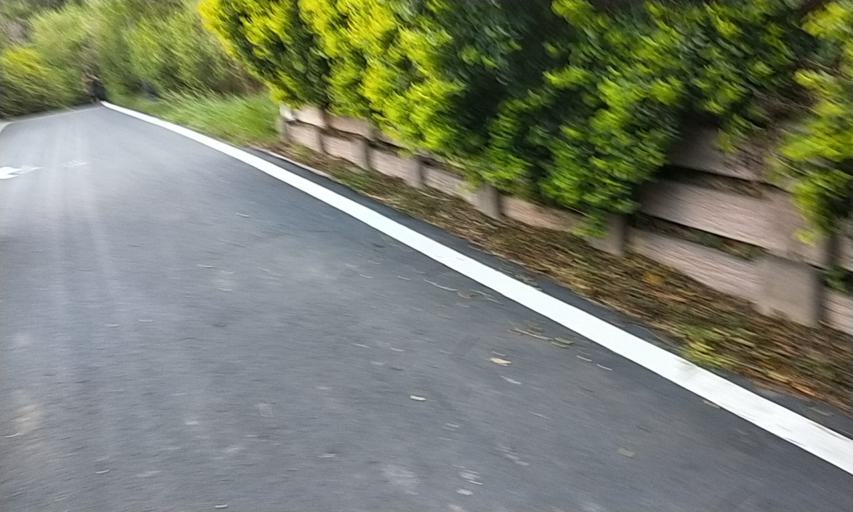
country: TW
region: Taiwan
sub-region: Hsinchu
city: Hsinchu
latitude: 24.7714
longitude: 120.9286
